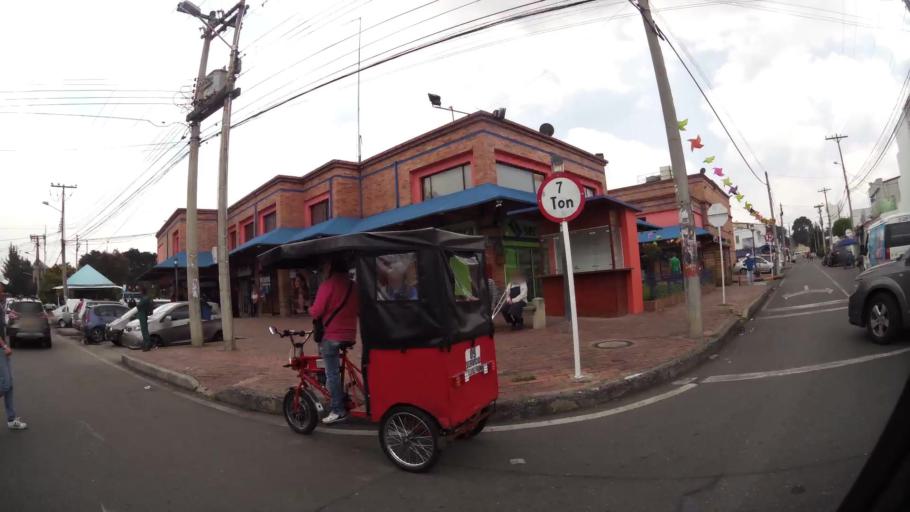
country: CO
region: Cundinamarca
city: Cota
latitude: 4.7543
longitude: -74.0546
